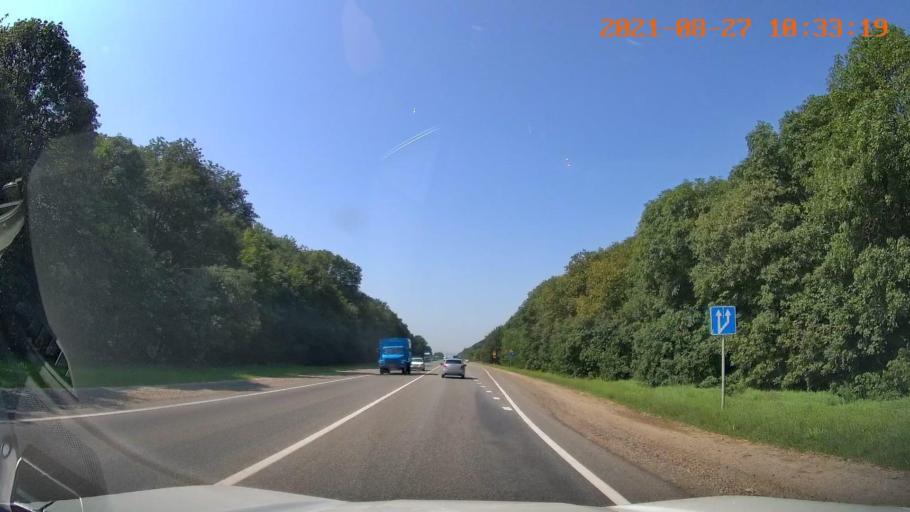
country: RU
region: Karachayevo-Cherkesiya
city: Cherkessk
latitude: 44.2606
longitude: 42.1221
